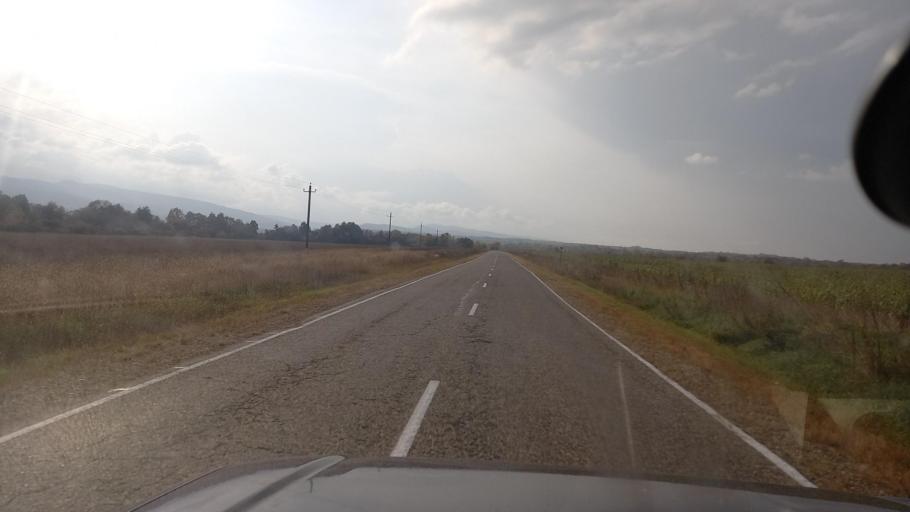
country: RU
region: Krasnodarskiy
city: Gubskaya
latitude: 44.3160
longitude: 40.5845
